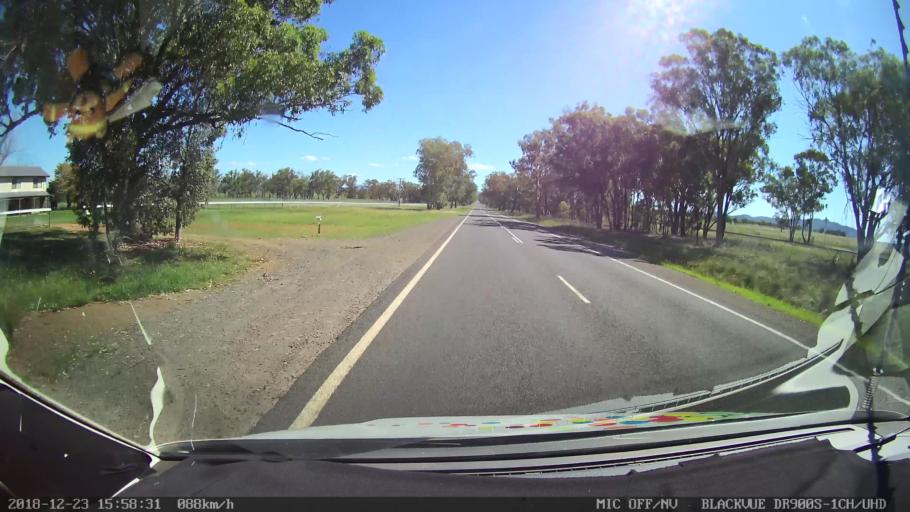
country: AU
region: New South Wales
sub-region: Tamworth Municipality
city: Phillip
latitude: -31.1892
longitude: 150.8410
